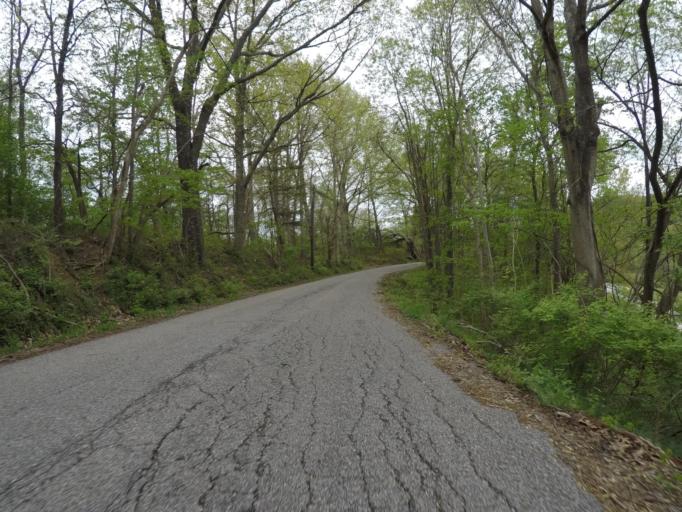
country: US
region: West Virginia
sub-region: Cabell County
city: Barboursville
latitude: 38.3931
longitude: -82.2506
